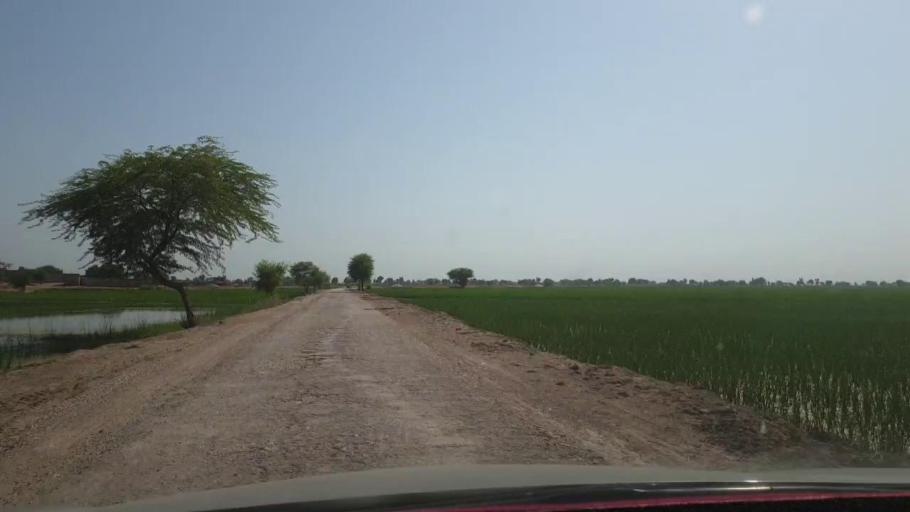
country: PK
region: Sindh
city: Nasirabad
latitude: 27.3599
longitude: 67.8505
